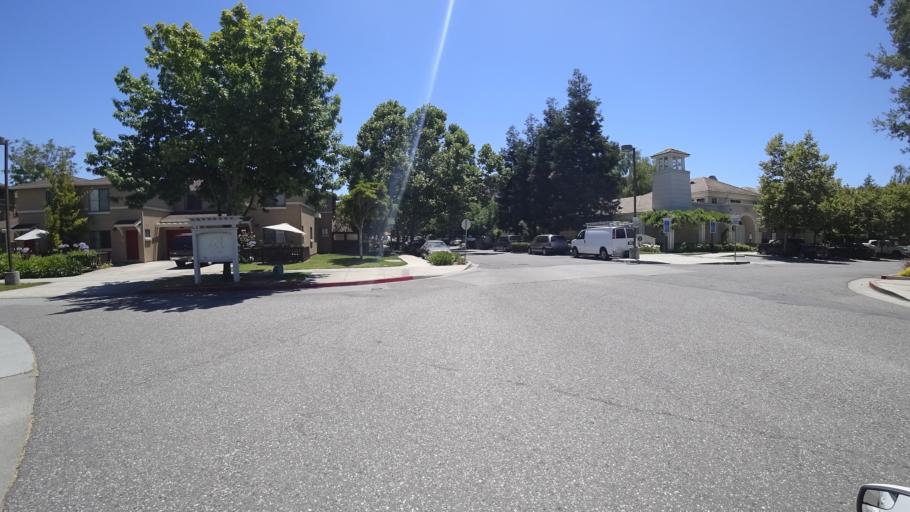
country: US
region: California
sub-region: Santa Clara County
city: Seven Trees
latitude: 37.2576
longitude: -121.8627
